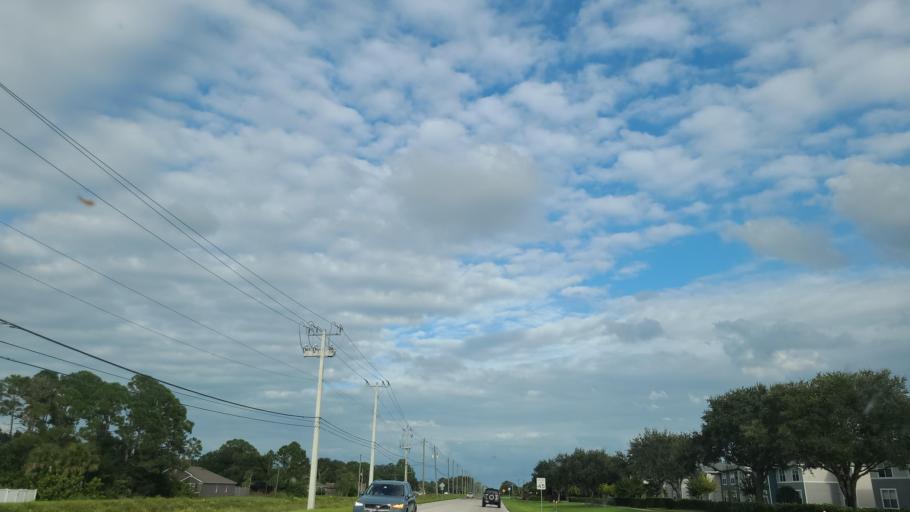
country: US
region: Florida
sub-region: Brevard County
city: June Park
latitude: 27.9990
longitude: -80.6883
